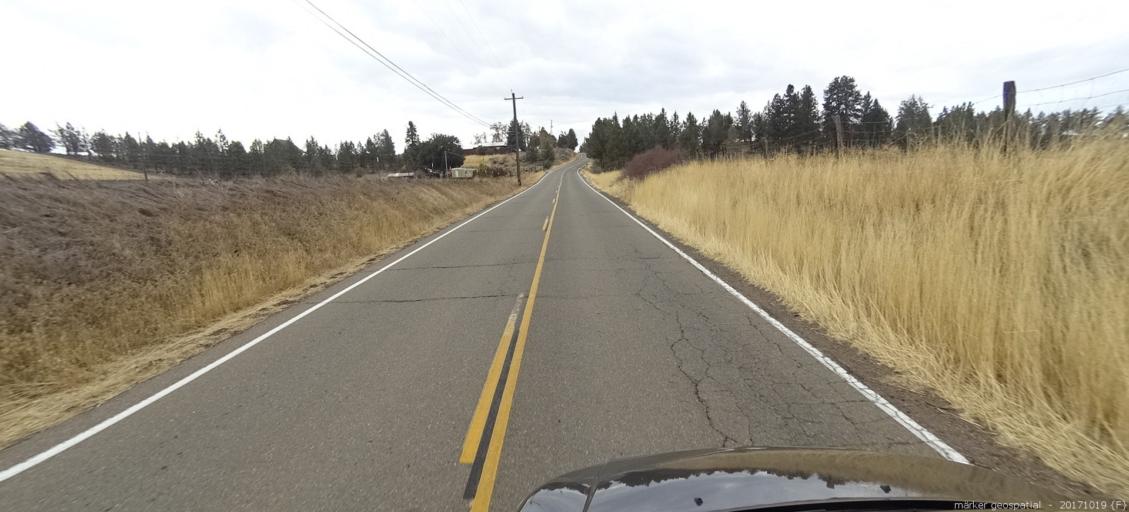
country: US
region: California
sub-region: Shasta County
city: Burney
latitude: 41.0421
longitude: -121.3314
